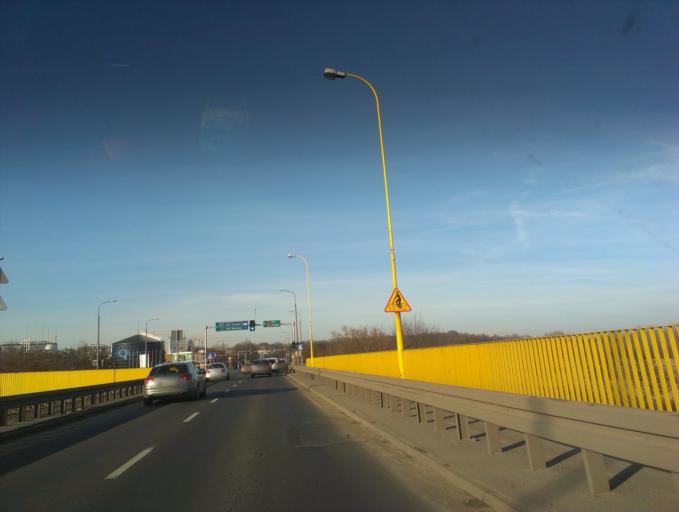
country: PL
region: Greater Poland Voivodeship
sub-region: Powiat poznanski
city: Czerwonak
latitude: 52.4294
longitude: 16.9633
